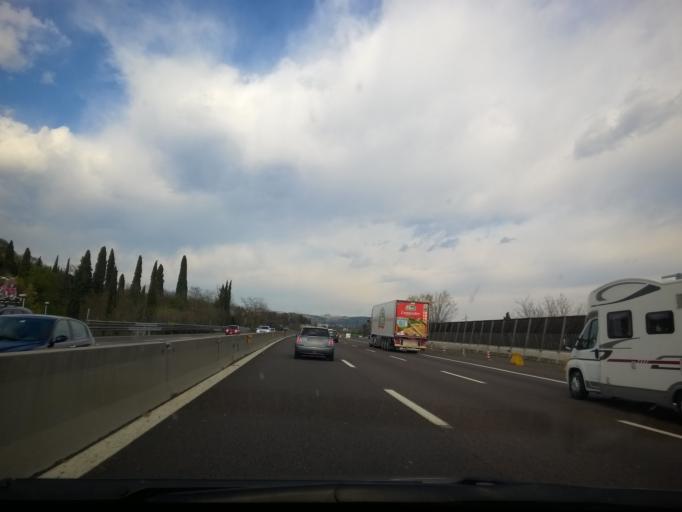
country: IT
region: Veneto
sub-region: Provincia di Verona
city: Monticelli-Fontana
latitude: 45.4203
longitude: 11.1219
